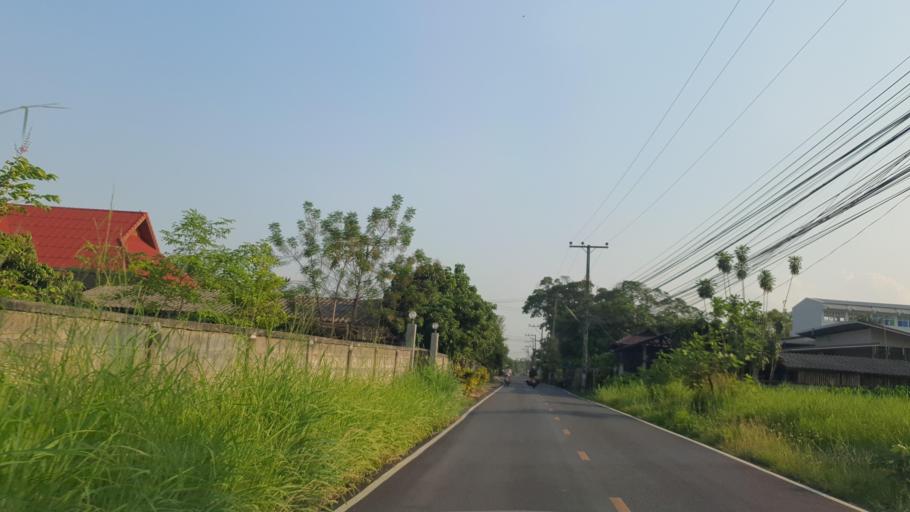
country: TH
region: Chiang Mai
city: Mae Wang
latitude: 18.6078
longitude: 98.8214
